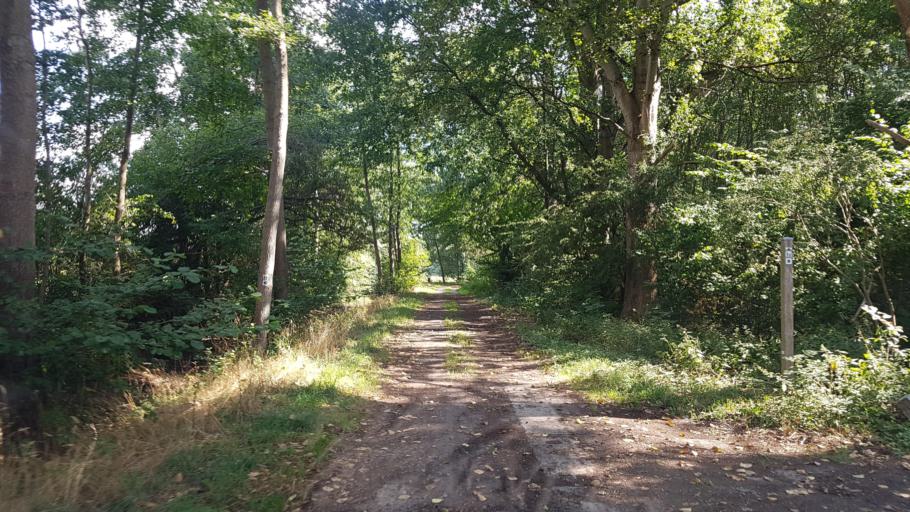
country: DE
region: Brandenburg
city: Bruck
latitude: 52.1930
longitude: 12.8094
